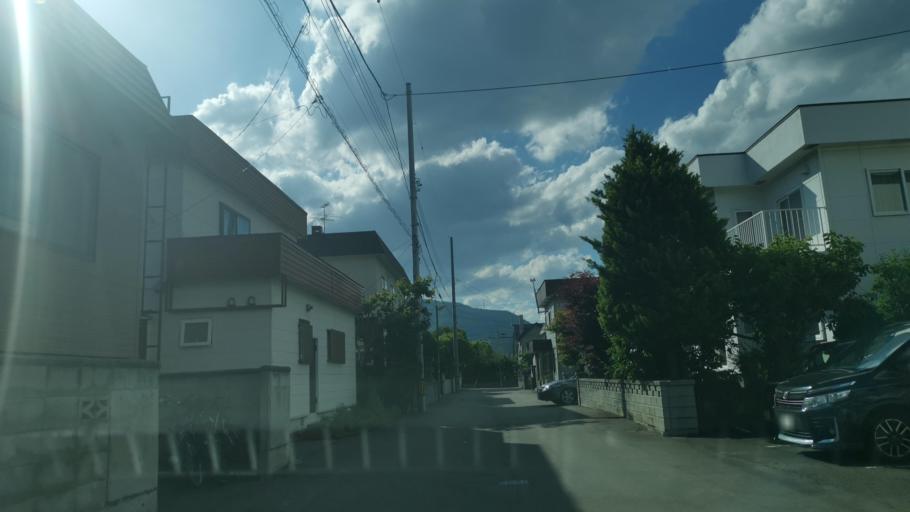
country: JP
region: Hokkaido
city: Sapporo
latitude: 43.0749
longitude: 141.2758
